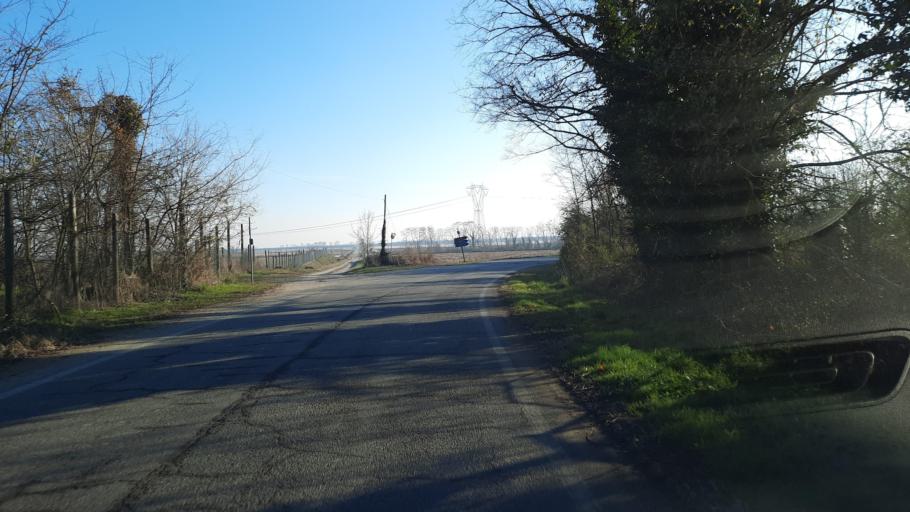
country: IT
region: Piedmont
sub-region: Provincia di Vercelli
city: Costanzana
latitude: 45.2213
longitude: 8.3652
